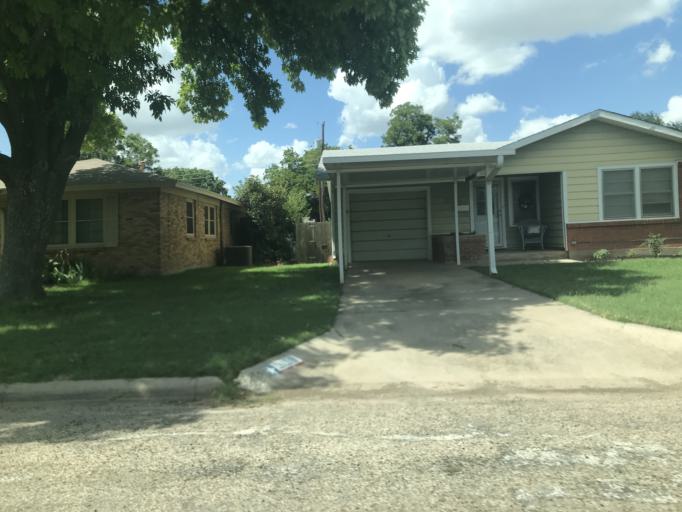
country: US
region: Texas
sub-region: Taylor County
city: Abilene
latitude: 32.4218
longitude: -99.7617
